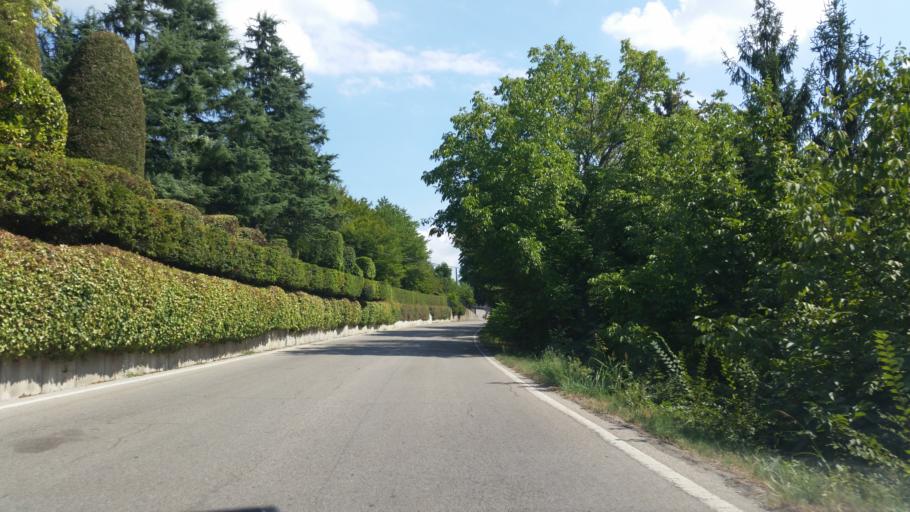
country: IT
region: Piedmont
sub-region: Provincia di Cuneo
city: Alba
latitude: 44.6958
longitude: 8.0476
